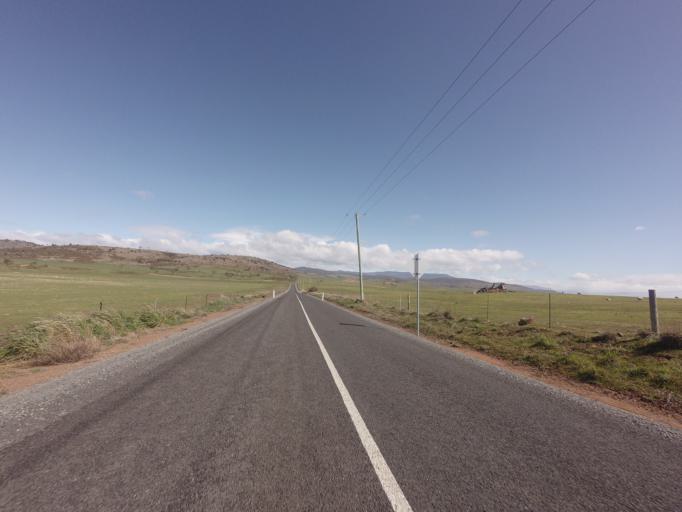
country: AU
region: Tasmania
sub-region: Northern Midlands
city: Evandale
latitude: -41.9090
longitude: 147.3847
